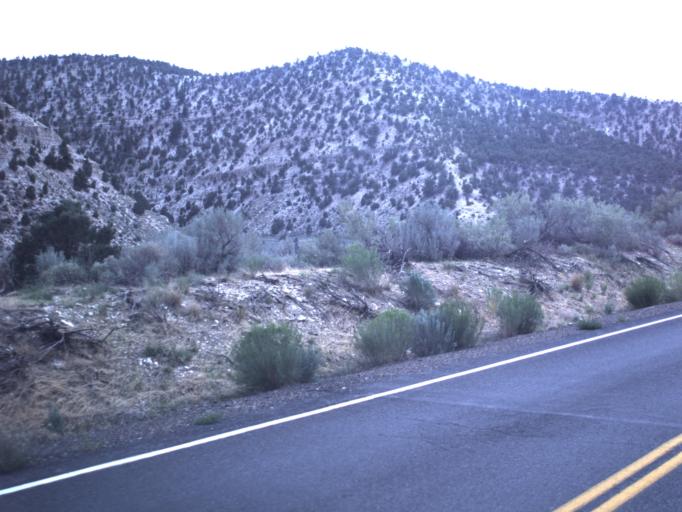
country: US
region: Utah
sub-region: Duchesne County
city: Duchesne
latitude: 40.0796
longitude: -110.5012
